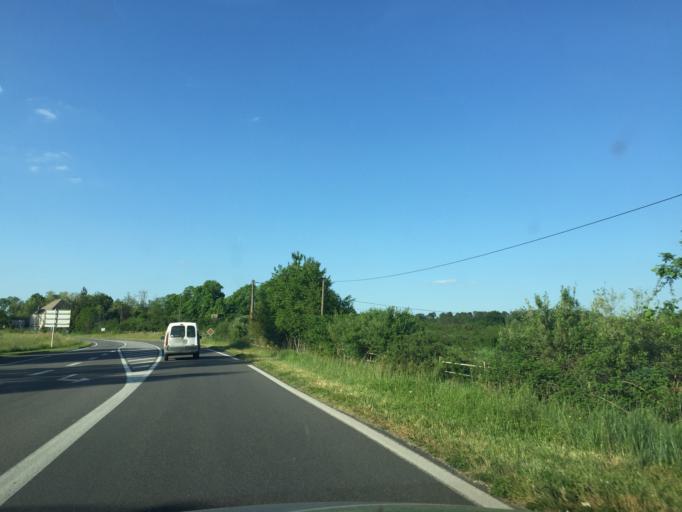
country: FR
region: Aquitaine
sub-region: Departement de la Gironde
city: Les Eglisottes-et-Chalaures
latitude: 45.1151
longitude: -0.0109
